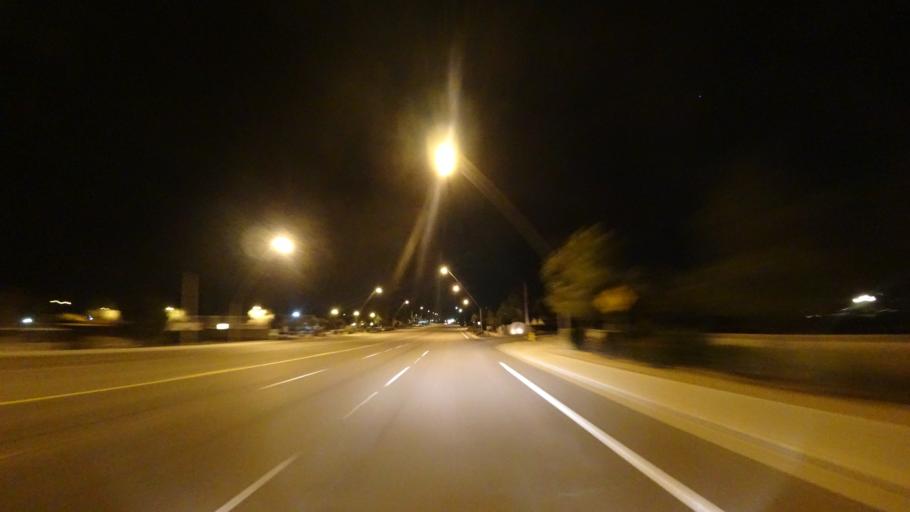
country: US
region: Arizona
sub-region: Maricopa County
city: Gilbert
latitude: 33.3621
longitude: -111.6878
